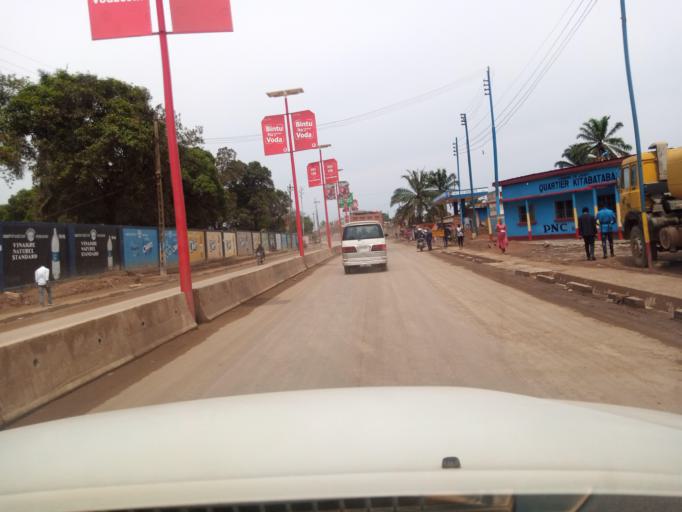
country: CD
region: Katanga
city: Likasi
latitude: -10.9871
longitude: 26.7636
